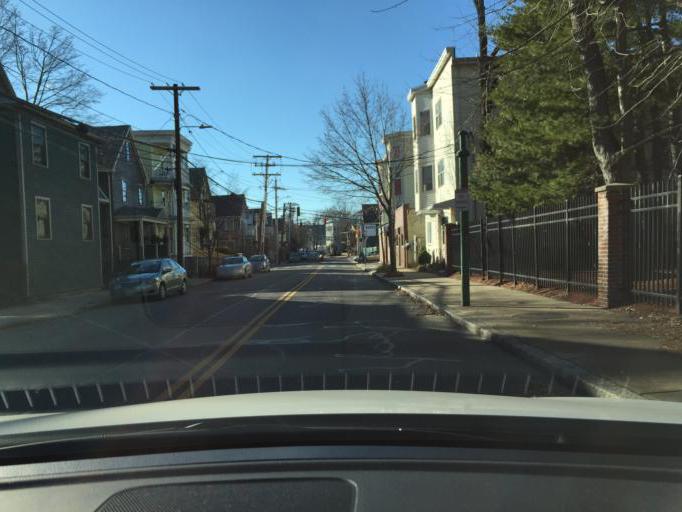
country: US
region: Massachusetts
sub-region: Middlesex County
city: Cambridge
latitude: 42.3865
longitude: -71.1302
